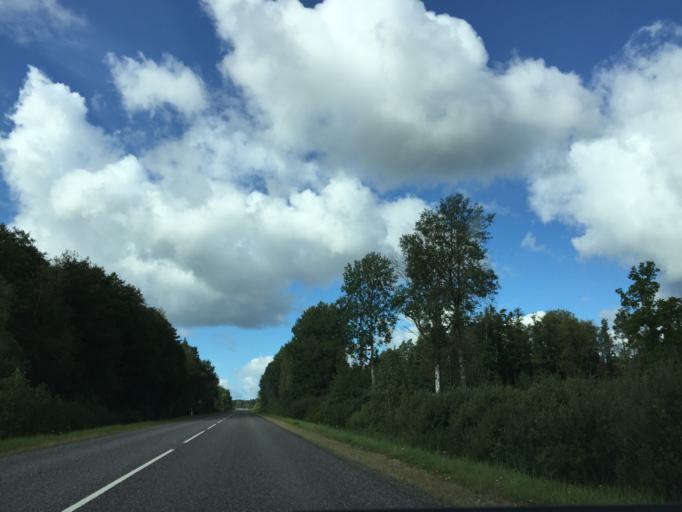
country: LV
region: Kuldigas Rajons
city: Kuldiga
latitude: 56.9948
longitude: 22.1127
